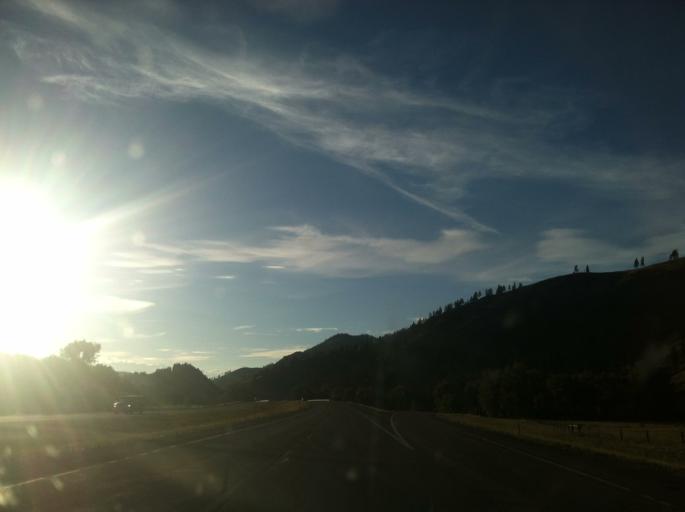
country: US
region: Montana
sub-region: Missoula County
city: Clinton
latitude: 46.6984
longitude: -113.4286
